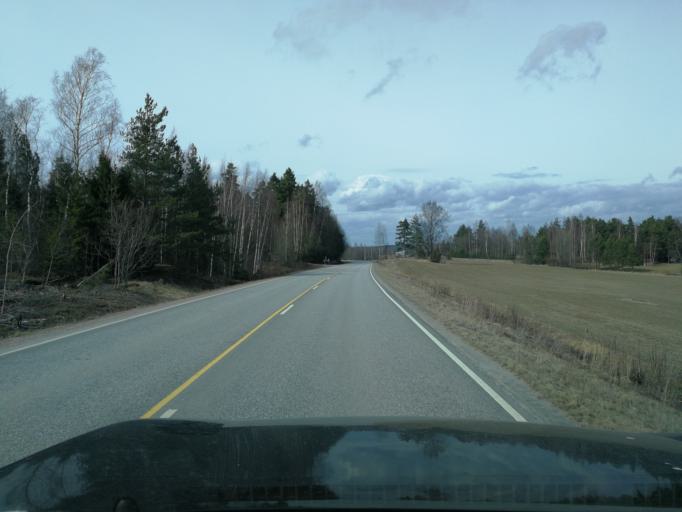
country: FI
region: Uusimaa
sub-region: Helsinki
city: Siuntio
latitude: 60.1036
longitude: 24.2481
